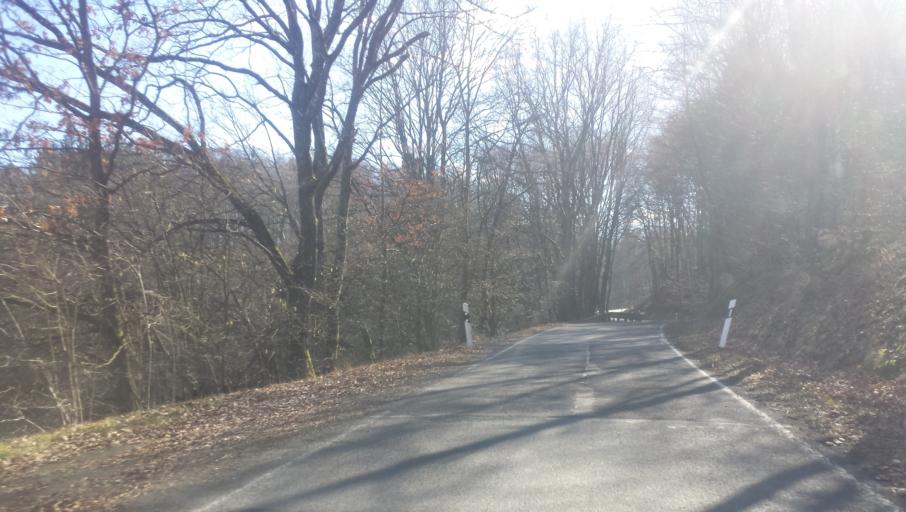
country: DE
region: Hesse
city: Gross-Bieberau
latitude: 49.7618
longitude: 8.8178
